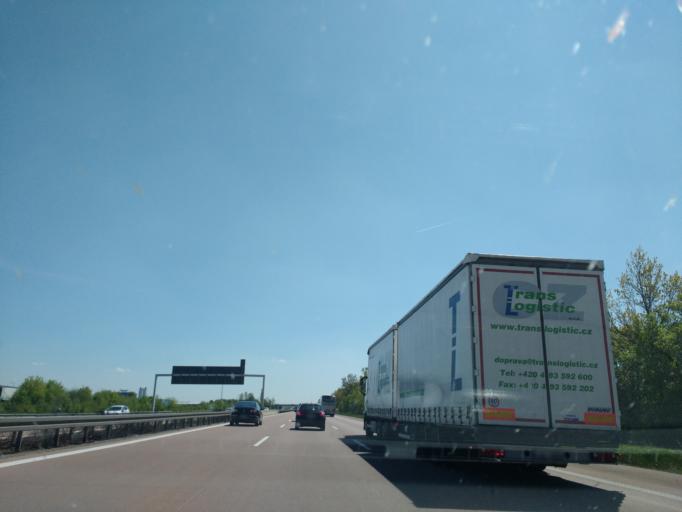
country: DE
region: Saxony-Anhalt
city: Dolbau
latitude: 51.4741
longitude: 12.0824
